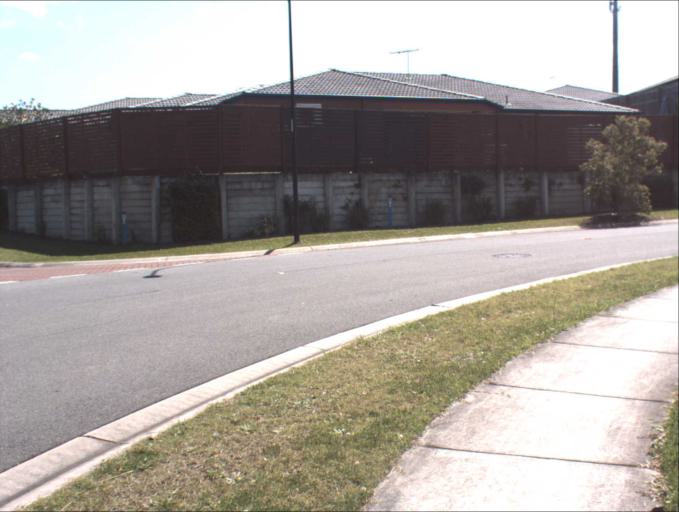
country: AU
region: Queensland
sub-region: Logan
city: Woodridge
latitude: -27.6588
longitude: 153.0802
